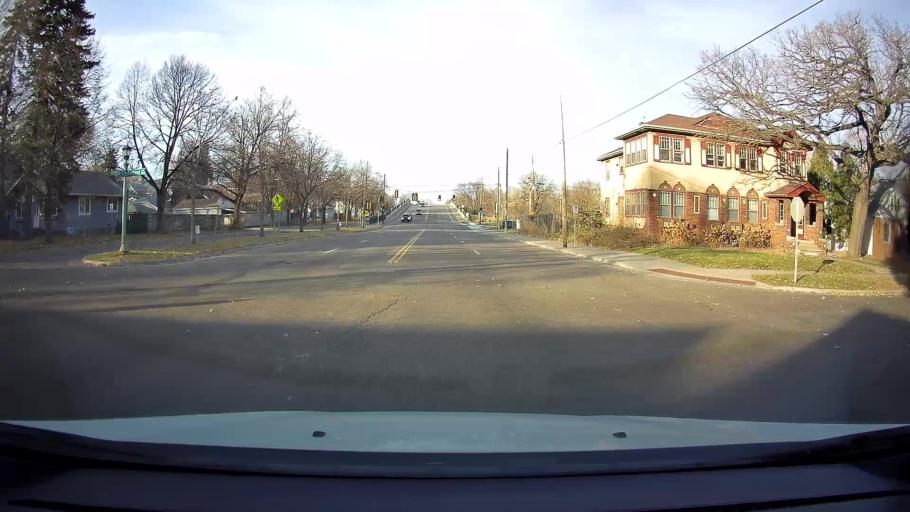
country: US
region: Minnesota
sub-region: Ramsey County
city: Falcon Heights
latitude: 44.9429
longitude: -93.1568
